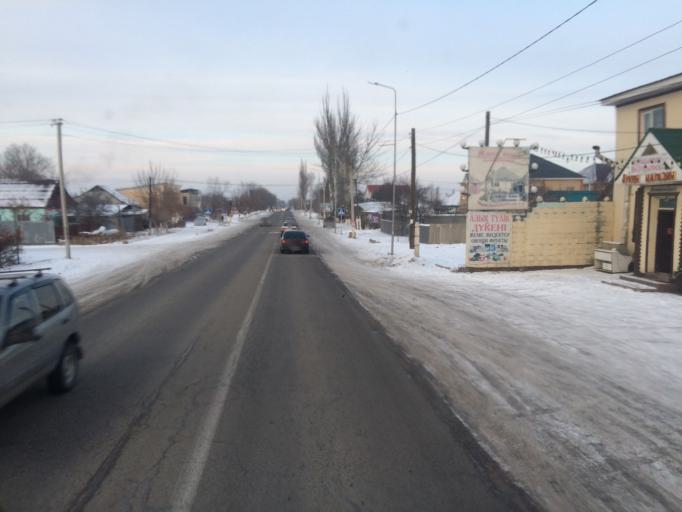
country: KZ
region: Almaty Oblysy
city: Burunday
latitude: 43.2675
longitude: 76.6703
